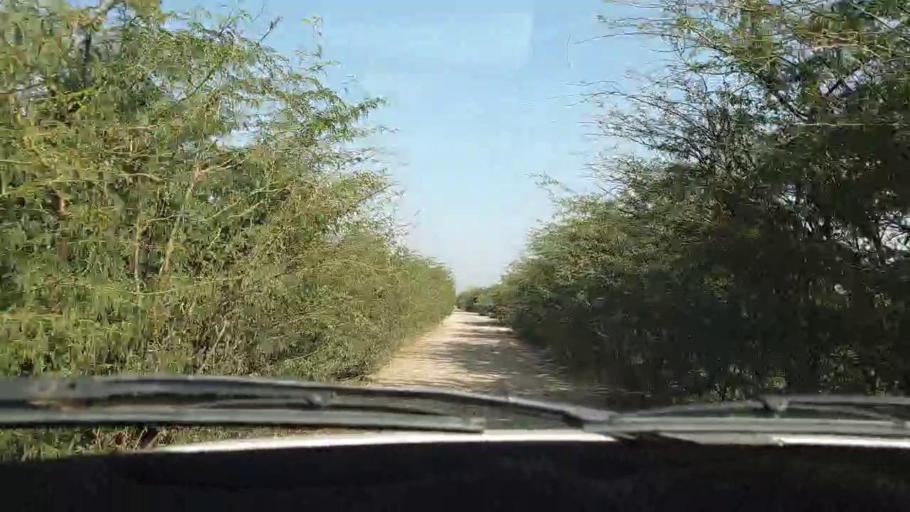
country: PK
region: Sindh
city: Tando Muhammad Khan
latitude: 24.9775
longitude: 68.4597
